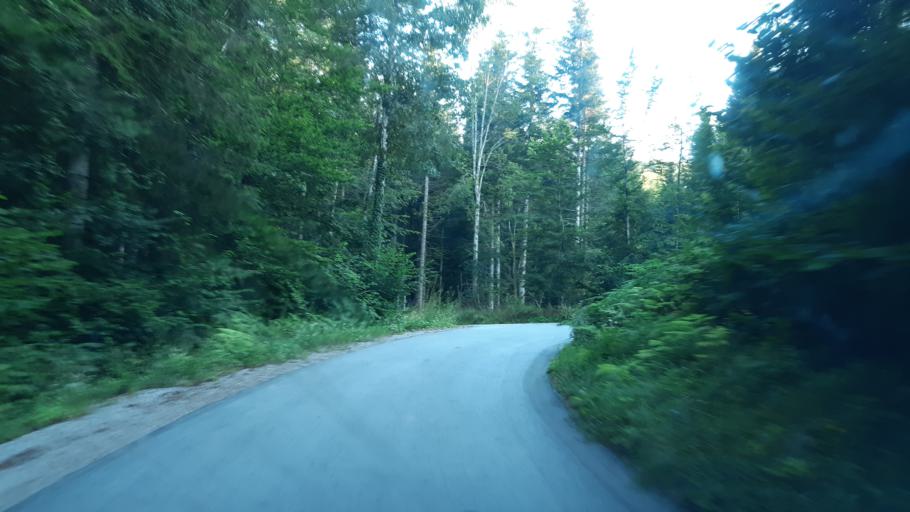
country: SI
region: Kocevje
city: Kocevje
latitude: 45.6626
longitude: 14.9139
